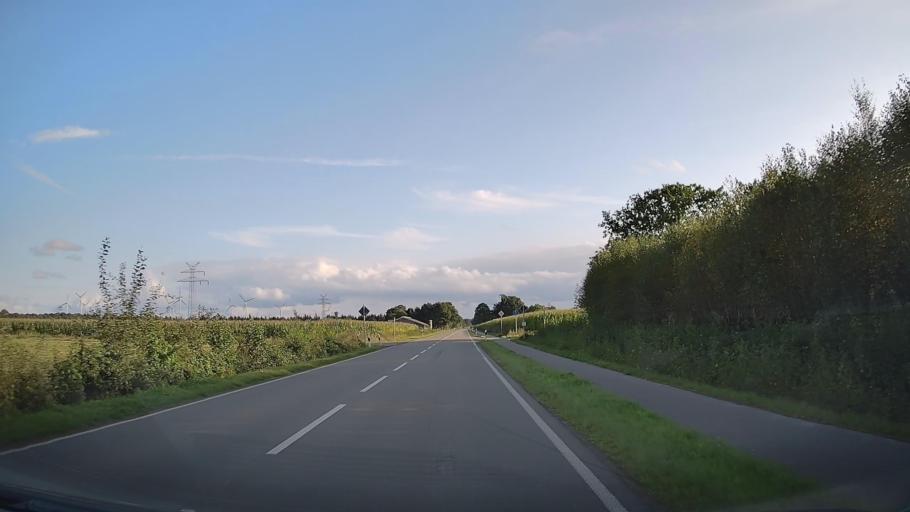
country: DE
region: Lower Saxony
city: Barssel
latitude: 53.1053
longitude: 7.7088
